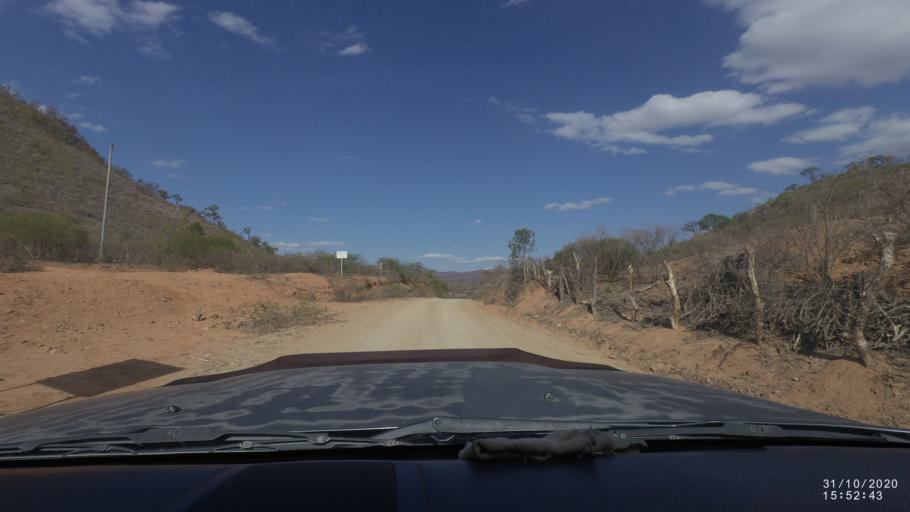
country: BO
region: Chuquisaca
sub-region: Provincia Zudanez
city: Mojocoya
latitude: -18.3190
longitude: -64.6917
